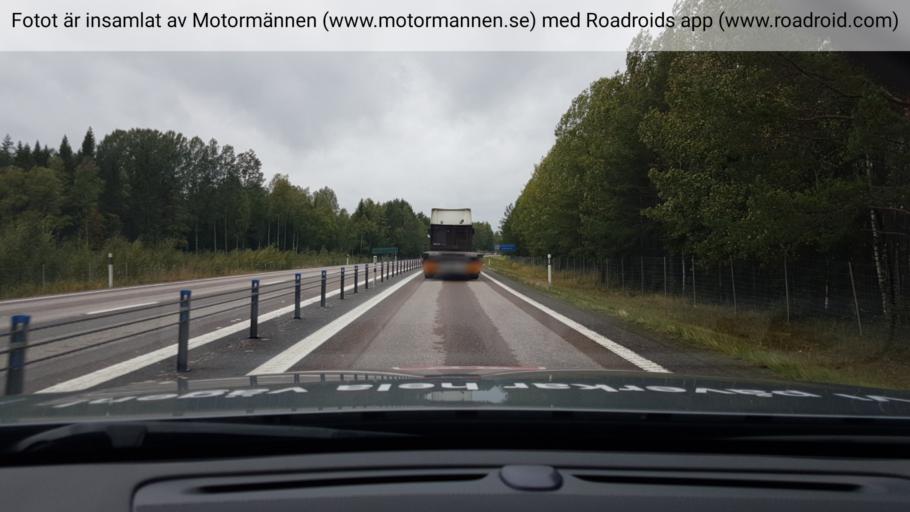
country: SE
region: Vaermland
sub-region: Kristinehamns Kommun
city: Kristinehamn
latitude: 59.3814
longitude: 13.8867
